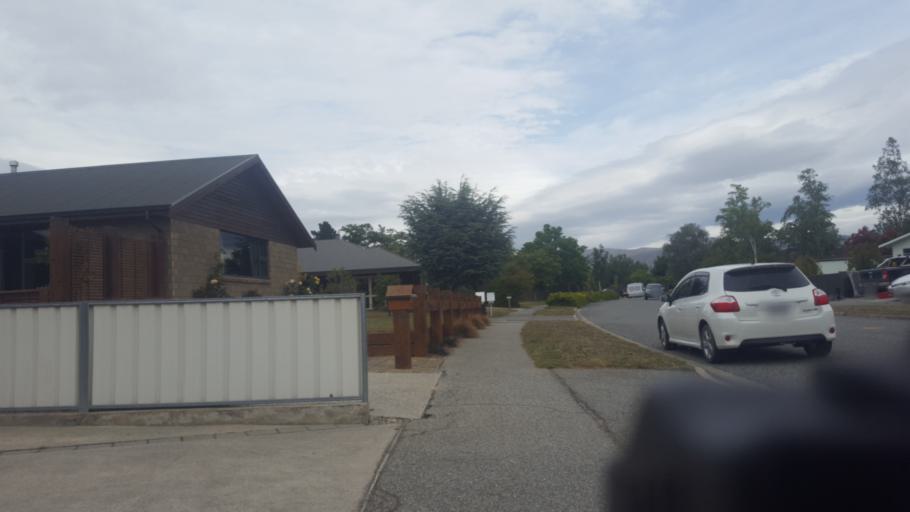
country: NZ
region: Otago
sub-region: Queenstown-Lakes District
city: Wanaka
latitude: -45.0405
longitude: 169.1928
